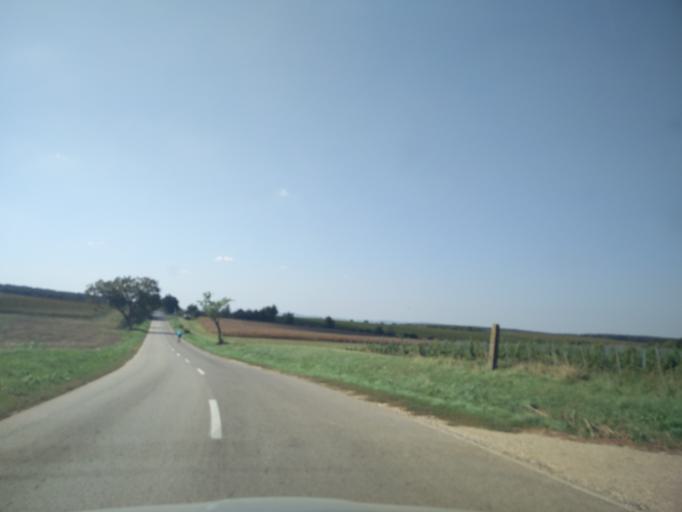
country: HU
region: Fejer
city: Etyek
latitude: 47.4453
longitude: 18.7202
